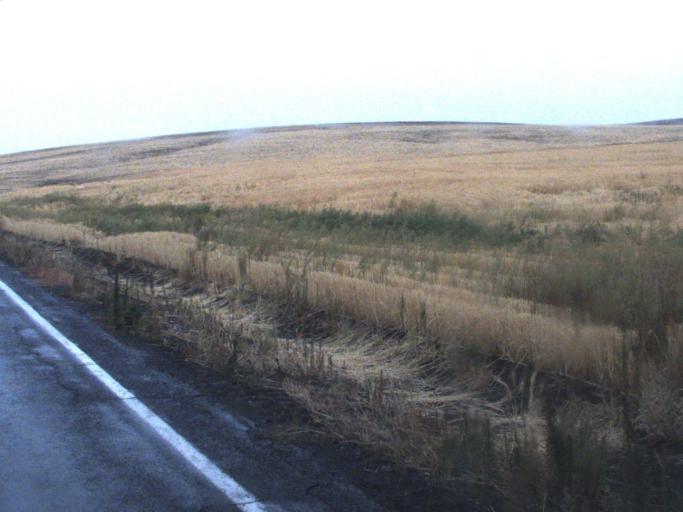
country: US
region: Washington
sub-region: Lincoln County
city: Davenport
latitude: 47.3788
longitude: -118.1242
